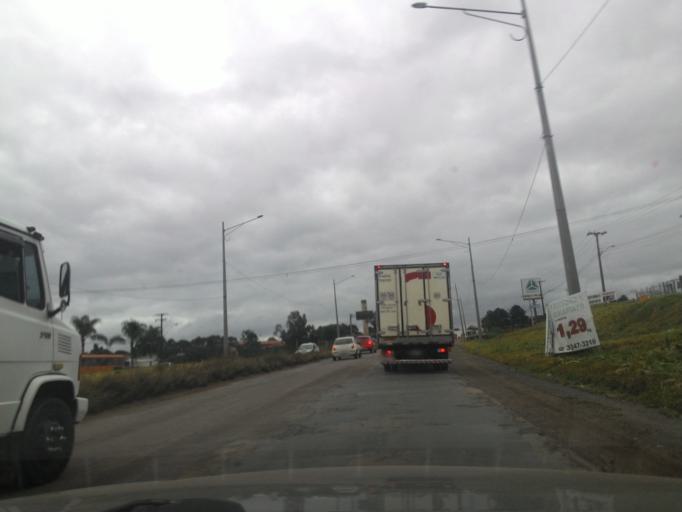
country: BR
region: Parana
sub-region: Sao Jose Dos Pinhais
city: Sao Jose dos Pinhais
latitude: -25.5351
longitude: -49.3010
